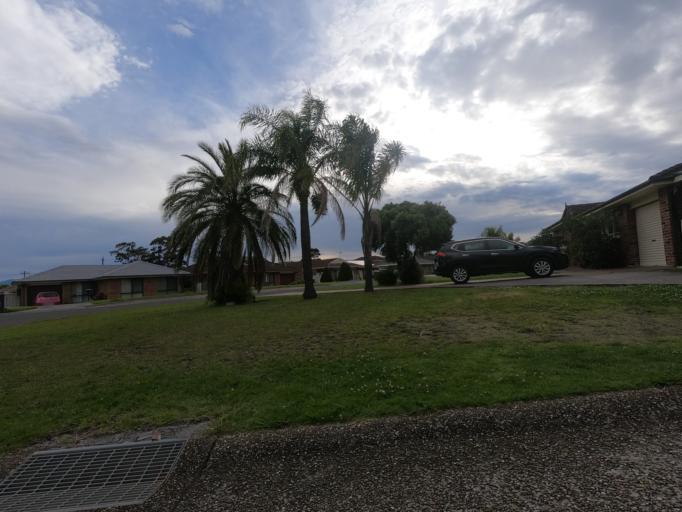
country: AU
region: New South Wales
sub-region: Wollongong
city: Berkeley
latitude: -34.4771
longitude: 150.8537
